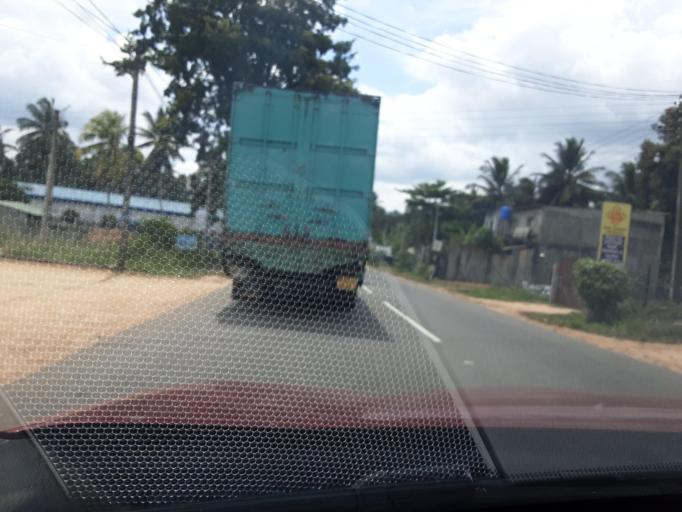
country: LK
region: North Western
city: Kuliyapitiya
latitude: 7.4483
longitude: 80.1998
